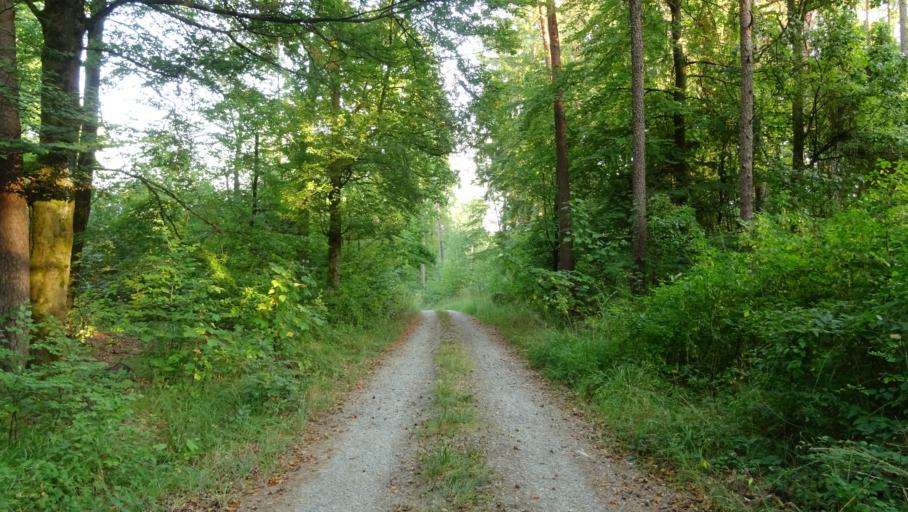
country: DE
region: Baden-Wuerttemberg
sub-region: Karlsruhe Region
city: Fahrenbach
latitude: 49.3932
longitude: 9.1593
